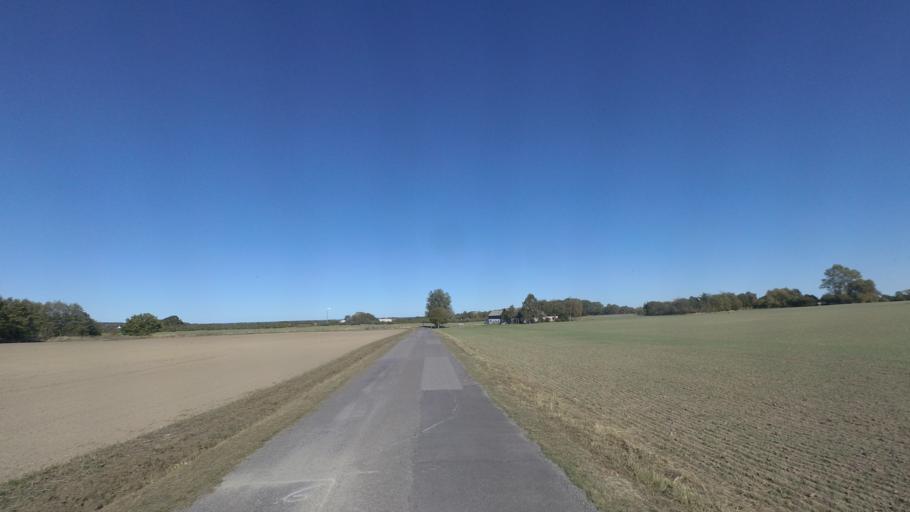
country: DK
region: Capital Region
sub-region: Bornholm Kommune
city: Nexo
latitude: 55.1195
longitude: 15.0472
